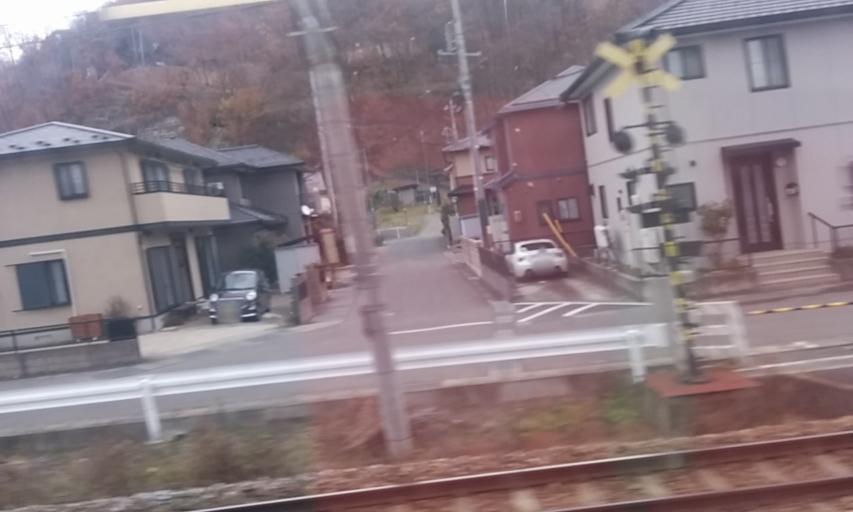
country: JP
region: Nagano
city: Nagano-shi
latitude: 36.5295
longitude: 138.1290
